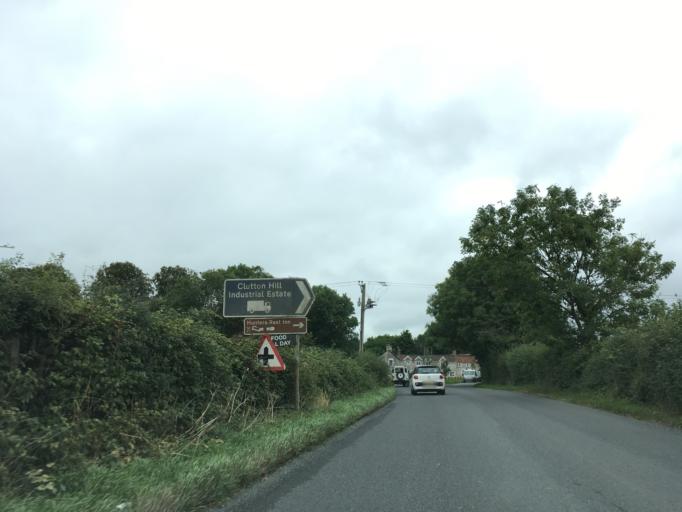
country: GB
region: England
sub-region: Bath and North East Somerset
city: Timsbury
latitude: 51.3359
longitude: -2.5086
